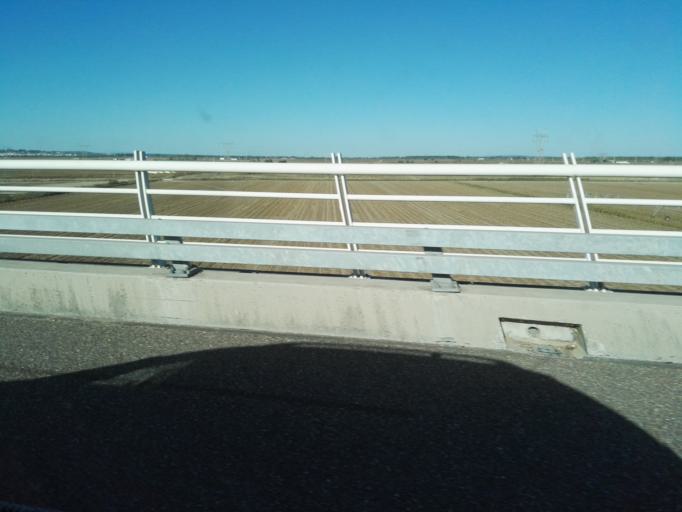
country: PT
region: Santarem
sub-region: Benavente
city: Samora Correia
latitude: 38.9900
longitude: -8.8941
